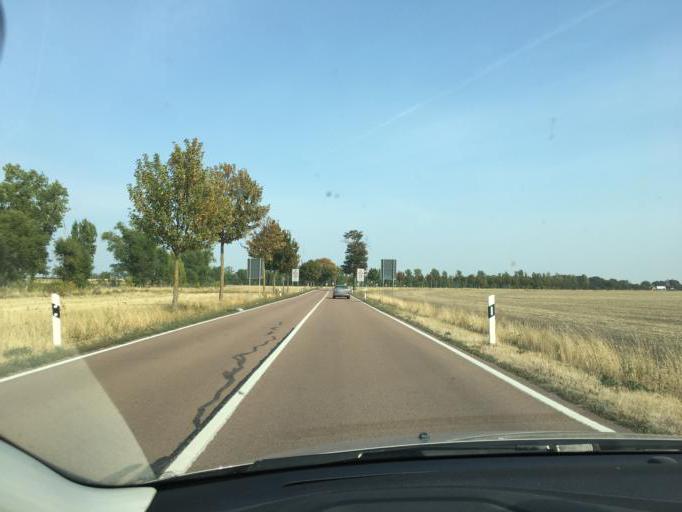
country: DE
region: Saxony-Anhalt
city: Wulfen
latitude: 51.7806
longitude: 11.8902
